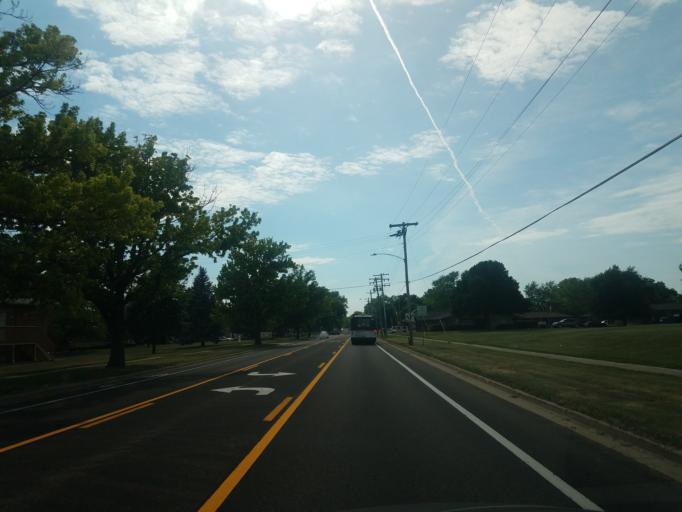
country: US
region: Illinois
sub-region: McLean County
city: Bloomington
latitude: 40.4801
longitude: -88.9576
